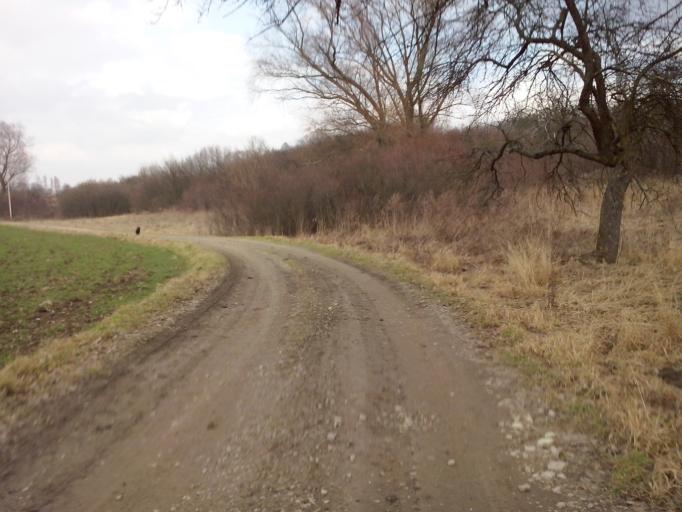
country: PL
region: Subcarpathian Voivodeship
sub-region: Powiat nizanski
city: Krzeszow
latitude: 50.4124
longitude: 22.3255
